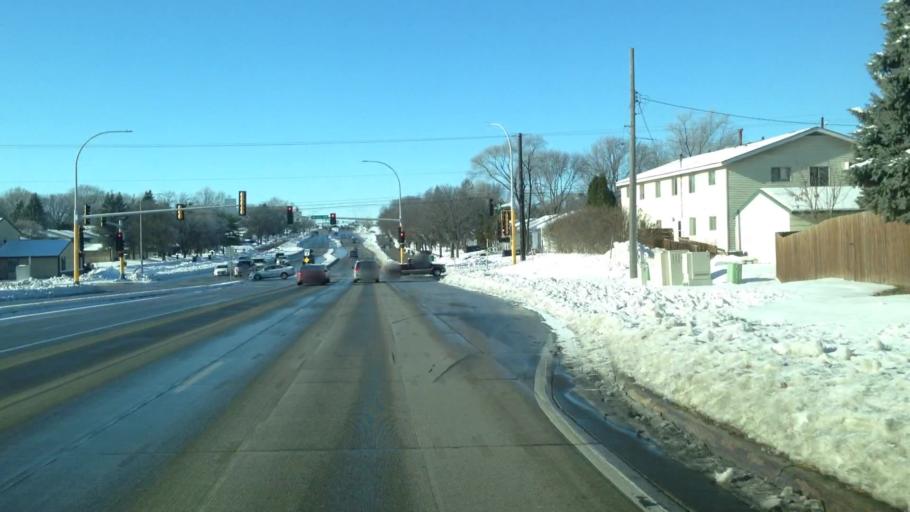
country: US
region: Minnesota
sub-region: Olmsted County
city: Rochester
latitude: 44.0617
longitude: -92.4877
